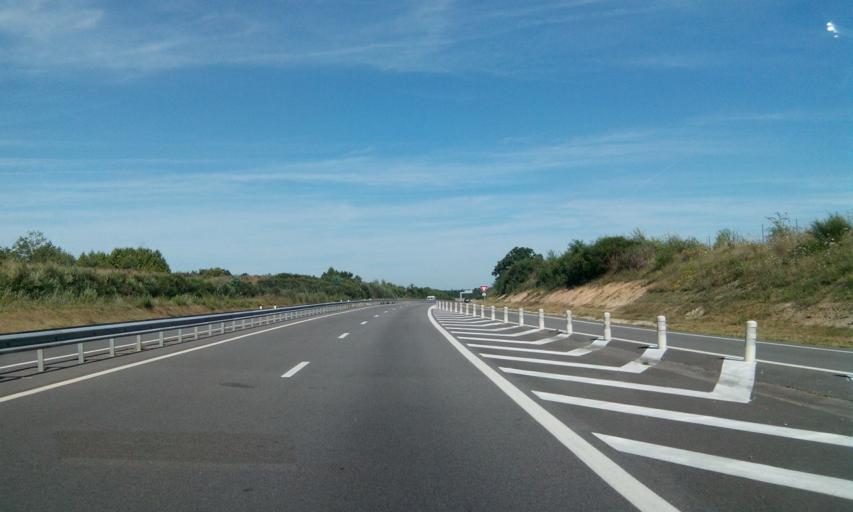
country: FR
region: Limousin
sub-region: Departement de la Haute-Vienne
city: Verneuil-sur-Vienne
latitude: 45.8594
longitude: 1.1436
